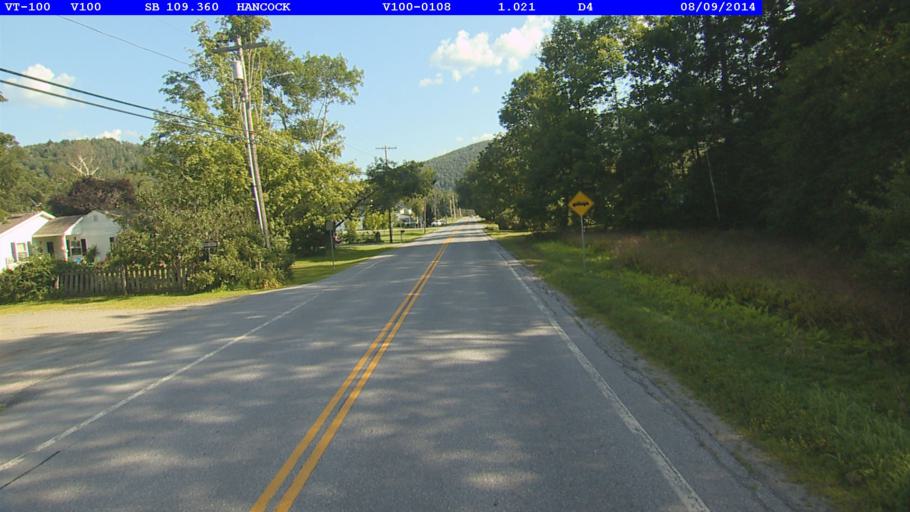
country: US
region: Vermont
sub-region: Orange County
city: Randolph
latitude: 43.9236
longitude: -72.8407
